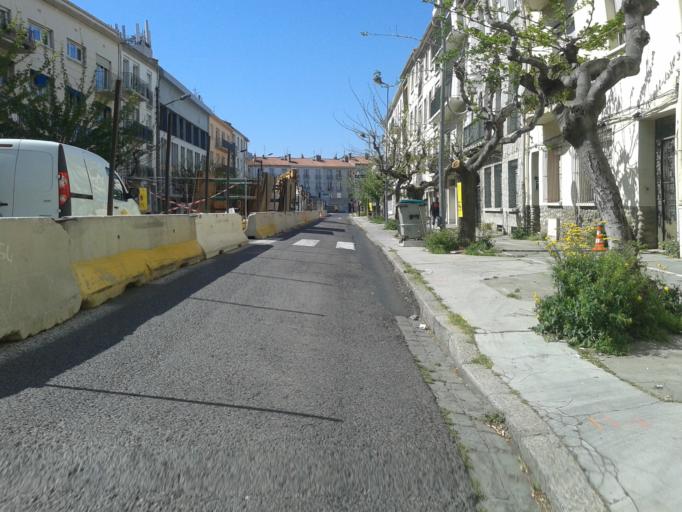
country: FR
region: Languedoc-Roussillon
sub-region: Departement des Pyrenees-Orientales
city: Perpignan
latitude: 42.6923
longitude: 2.8993
